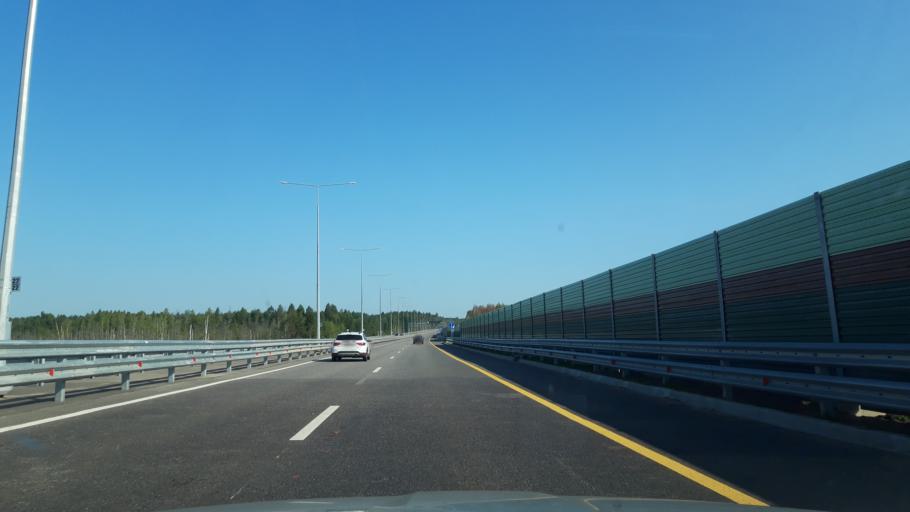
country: RU
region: Moskovskaya
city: Reshetnikovo
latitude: 56.4298
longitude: 36.5471
